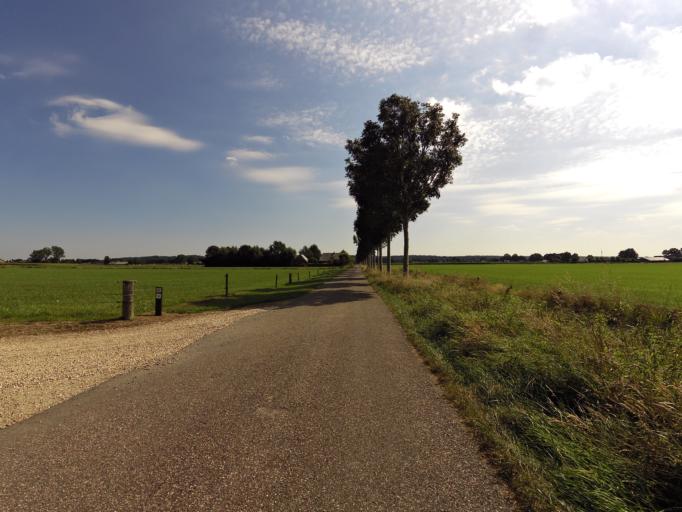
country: NL
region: Gelderland
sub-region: Gemeente Montferland
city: s-Heerenberg
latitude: 51.9304
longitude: 6.1850
